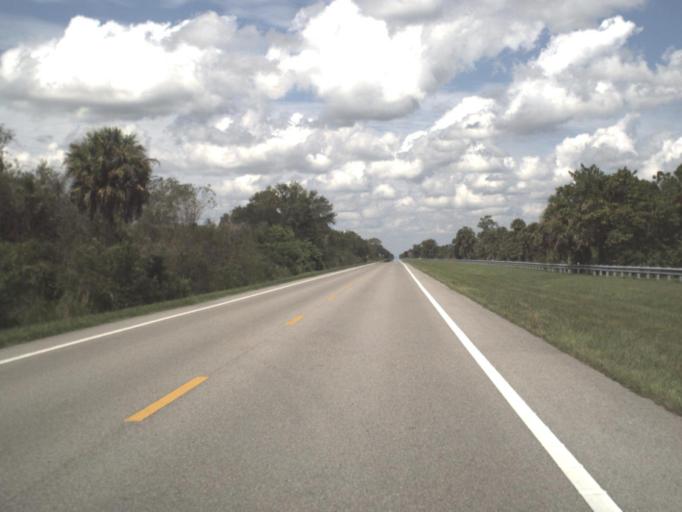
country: US
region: Florida
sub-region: Collier County
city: Immokalee
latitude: 26.2787
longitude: -81.3423
